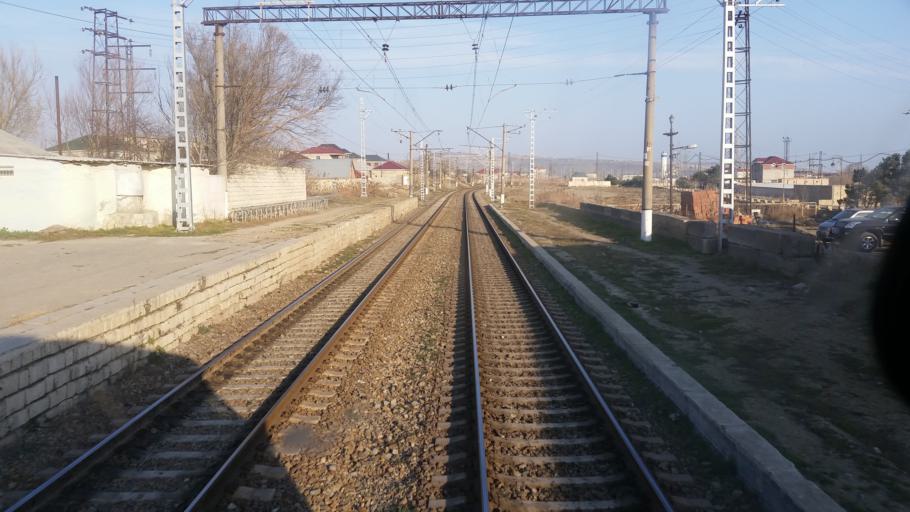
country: AZ
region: Baki
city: Lokbatan
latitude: 40.3176
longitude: 49.7276
